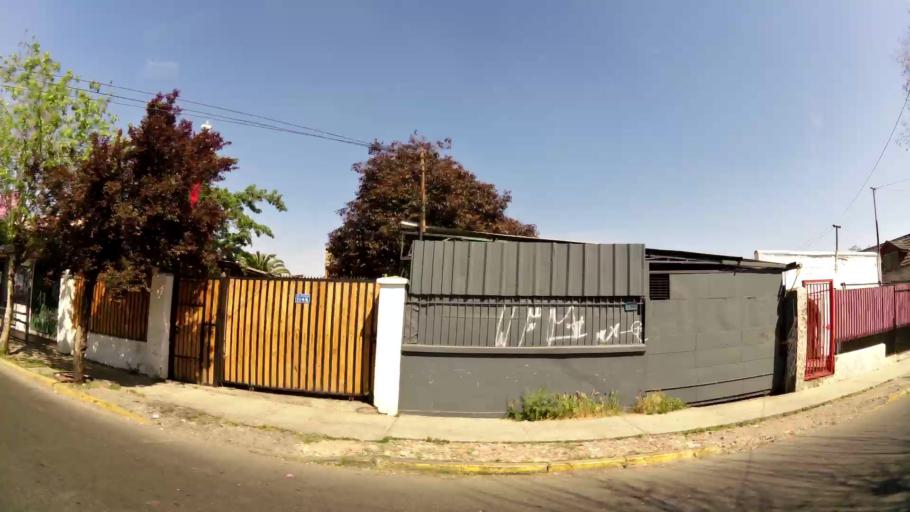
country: CL
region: Santiago Metropolitan
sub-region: Provincia de Santiago
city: La Pintana
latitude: -33.5286
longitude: -70.6483
